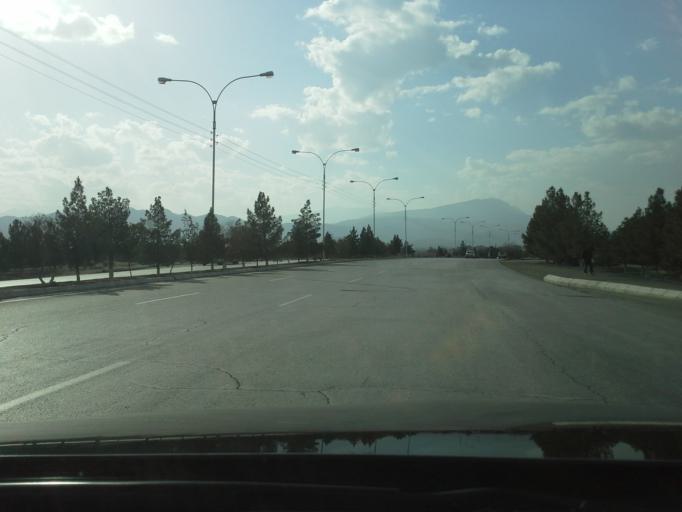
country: TM
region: Ahal
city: Abadan
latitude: 37.9710
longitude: 58.2642
